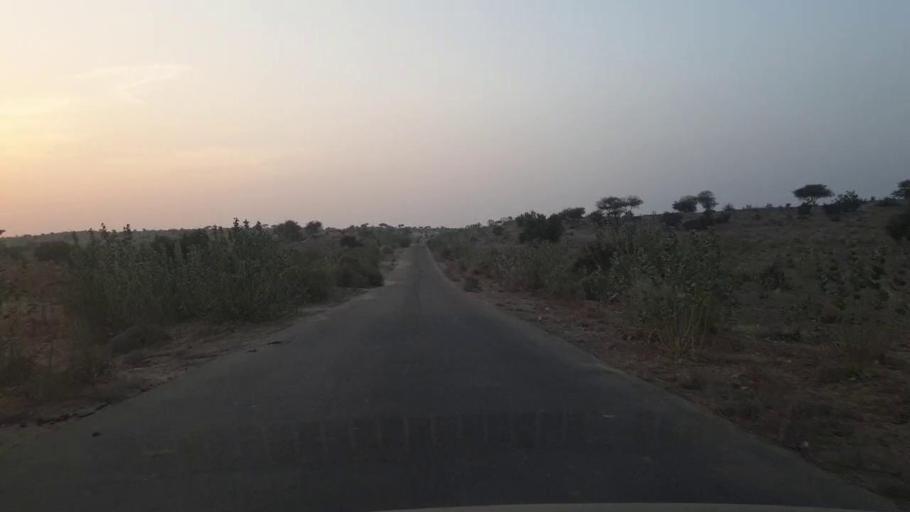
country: PK
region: Sindh
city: Umarkot
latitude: 25.3089
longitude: 70.0668
